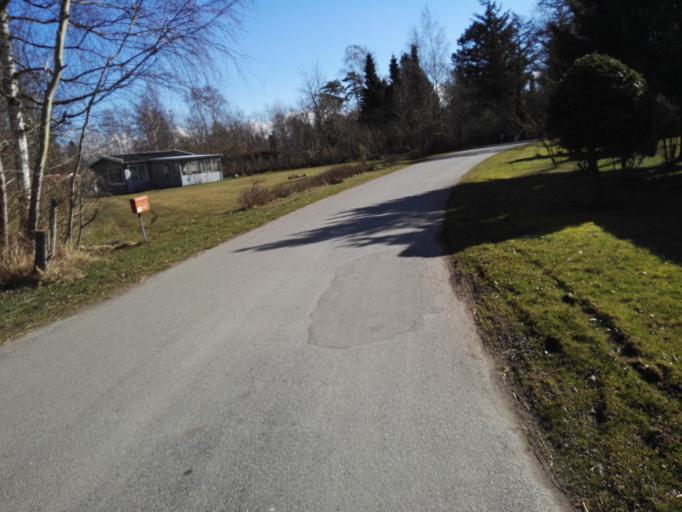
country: DK
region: Zealand
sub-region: Lejre Kommune
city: Ejby
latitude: 55.7791
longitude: 11.8099
